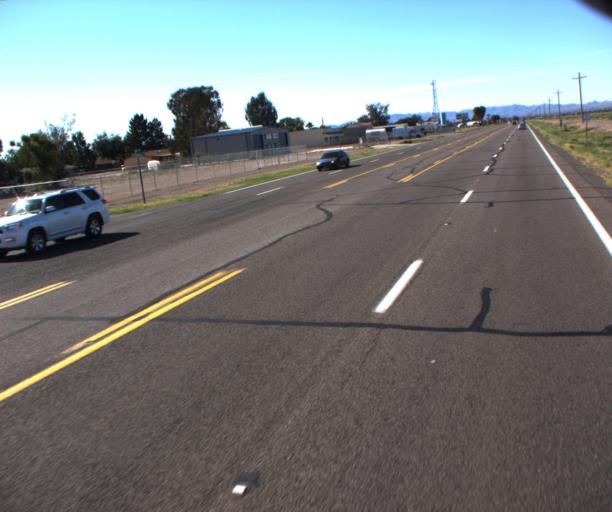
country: US
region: Arizona
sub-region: Mohave County
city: Willow Valley
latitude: 34.9062
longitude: -114.5980
